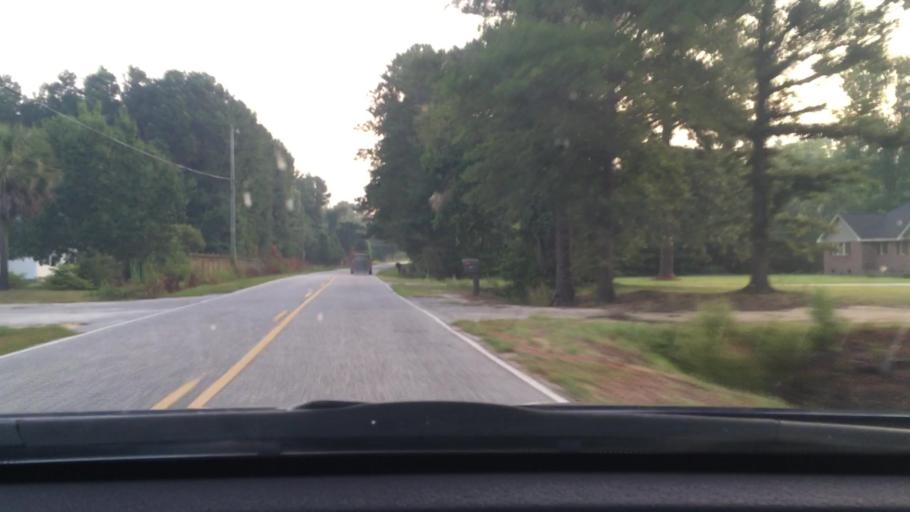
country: US
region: South Carolina
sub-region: Darlington County
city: Hartsville
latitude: 34.3348
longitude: -80.1022
